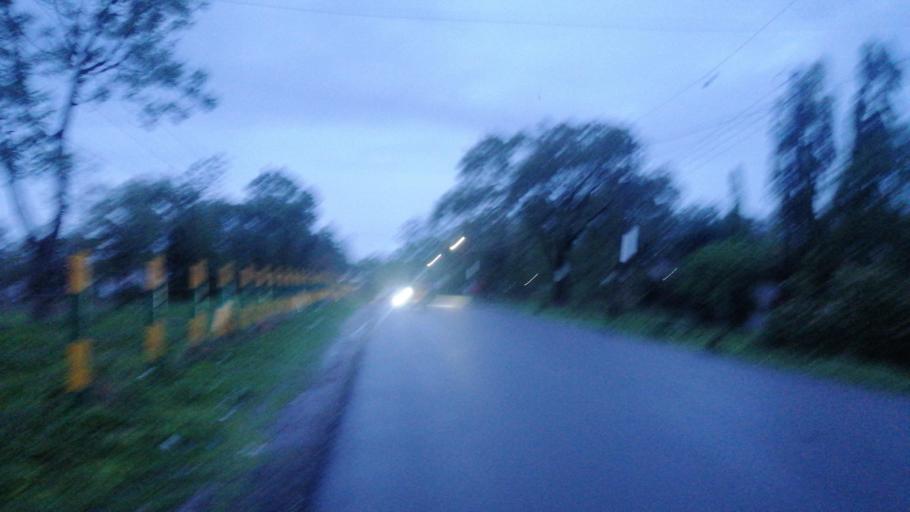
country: IN
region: Maharashtra
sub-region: Aurangabad Division
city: Aurangabad
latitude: 19.8769
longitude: 75.3768
